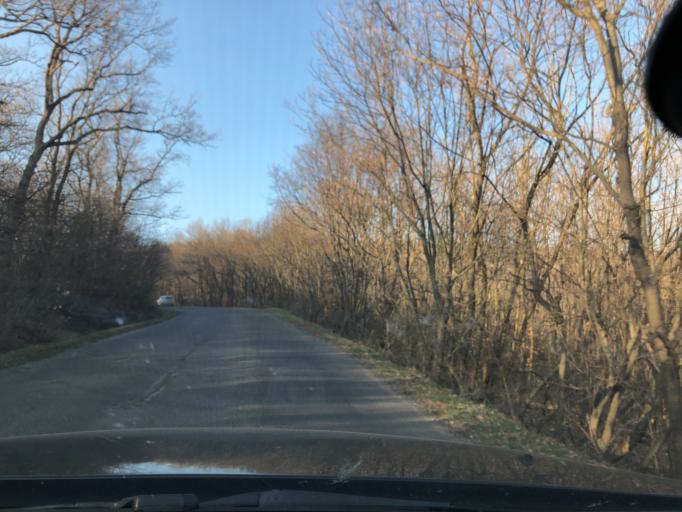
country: HU
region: Nograd
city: Paszto
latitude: 47.9216
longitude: 19.6316
